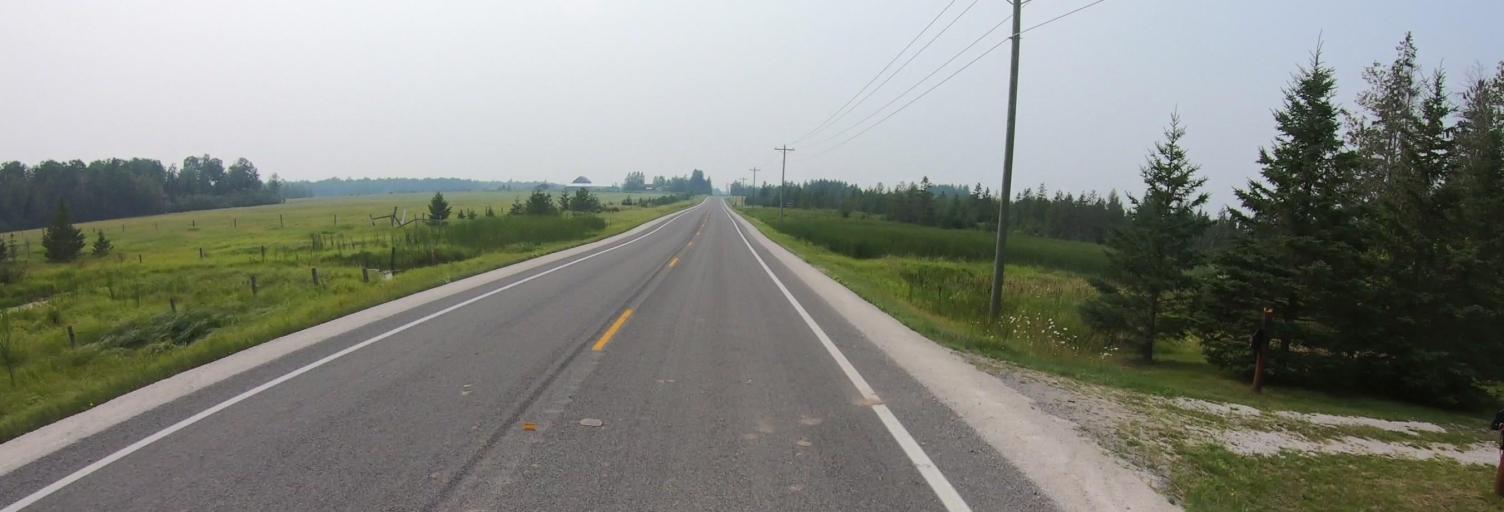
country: US
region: Michigan
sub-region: Chippewa County
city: Sault Ste. Marie
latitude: 46.0716
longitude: -84.2294
